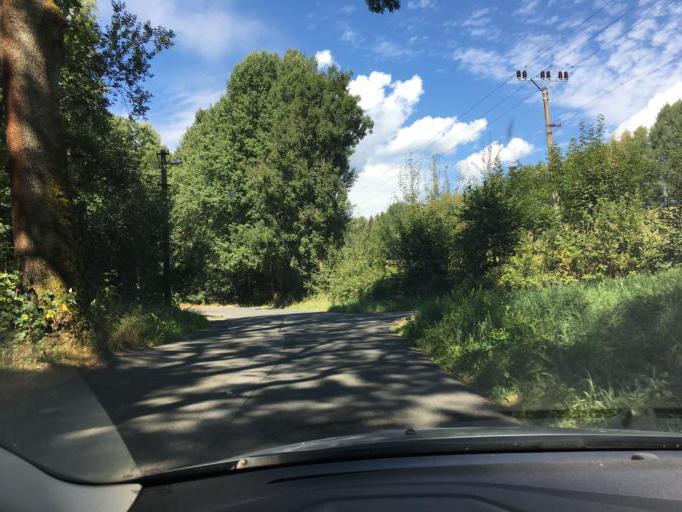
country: CZ
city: Plavy
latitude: 50.7034
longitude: 15.3492
